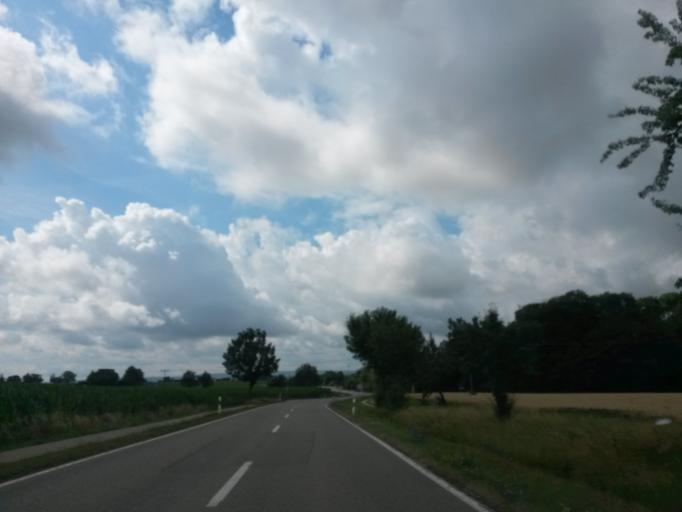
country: DE
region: Baden-Wuerttemberg
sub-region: Regierungsbezirk Stuttgart
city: Ellwangen
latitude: 48.9660
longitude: 10.1639
